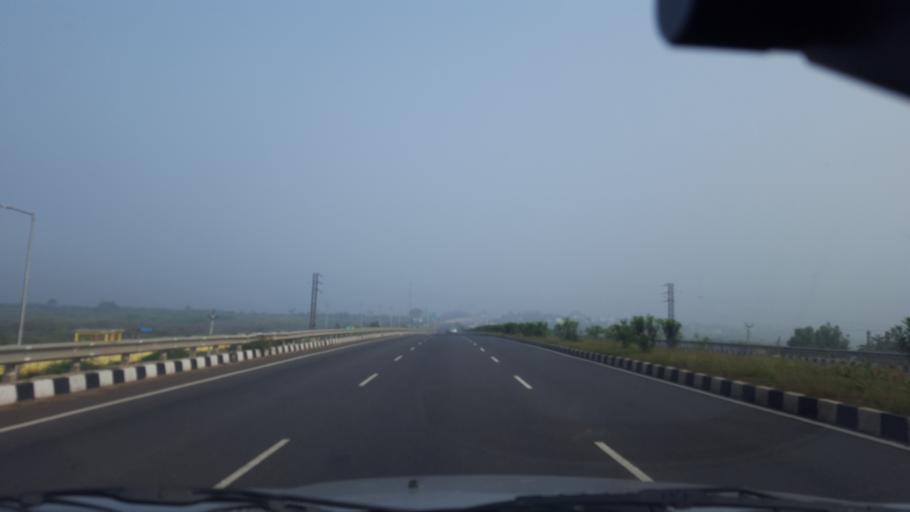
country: IN
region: Andhra Pradesh
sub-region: Prakasam
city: Ongole
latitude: 15.4141
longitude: 80.0392
